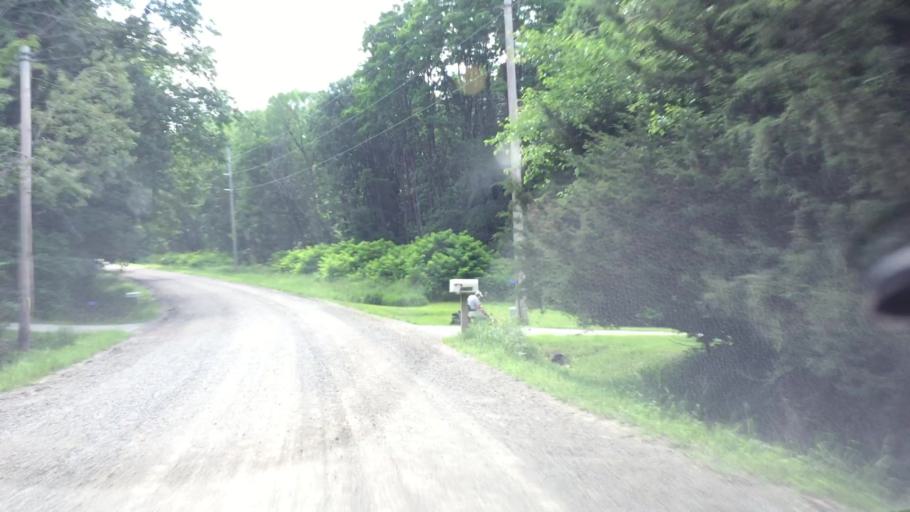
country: US
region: Iowa
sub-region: Linn County
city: Ely
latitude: 41.8311
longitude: -91.6166
